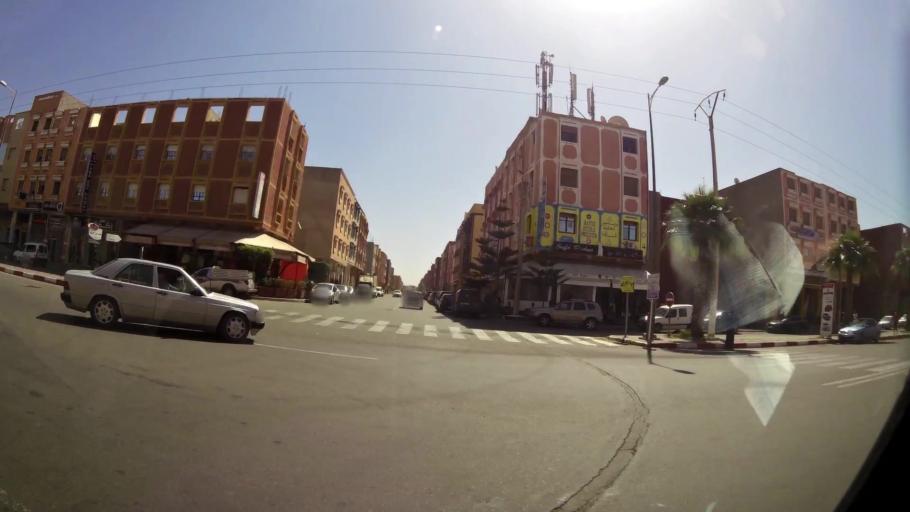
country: MA
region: Souss-Massa-Draa
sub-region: Inezgane-Ait Mellou
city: Inezgane
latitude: 30.3356
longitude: -9.5042
